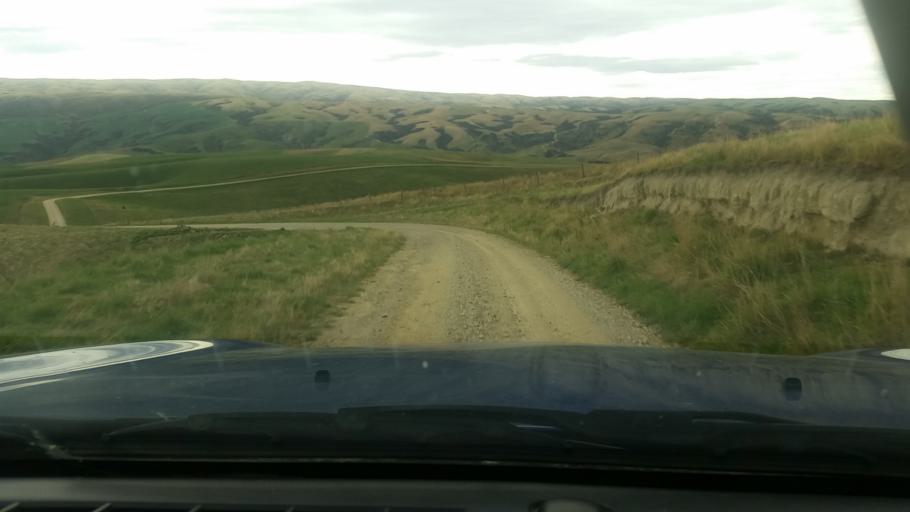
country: NZ
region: Otago
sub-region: Clutha District
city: Balclutha
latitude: -45.7089
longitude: 169.5225
